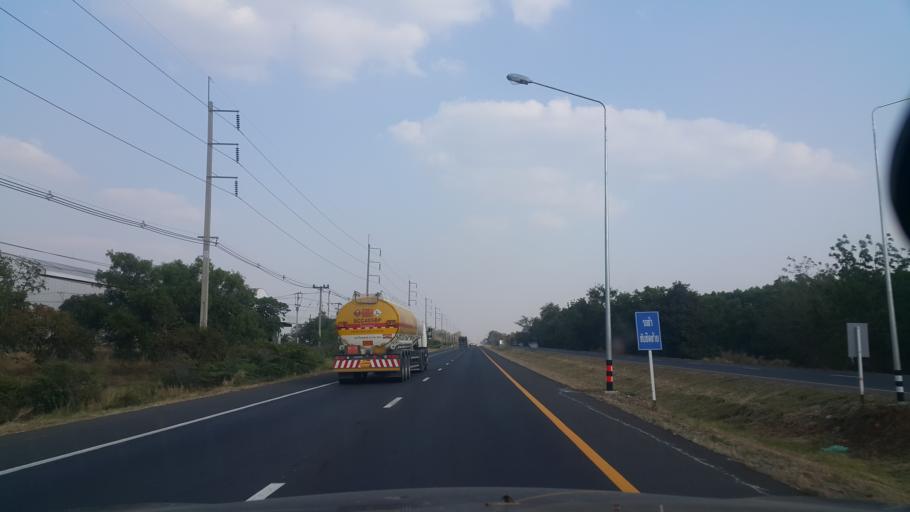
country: TH
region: Buriram
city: Chaloem Phra Kiat
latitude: 14.6214
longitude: 102.8885
